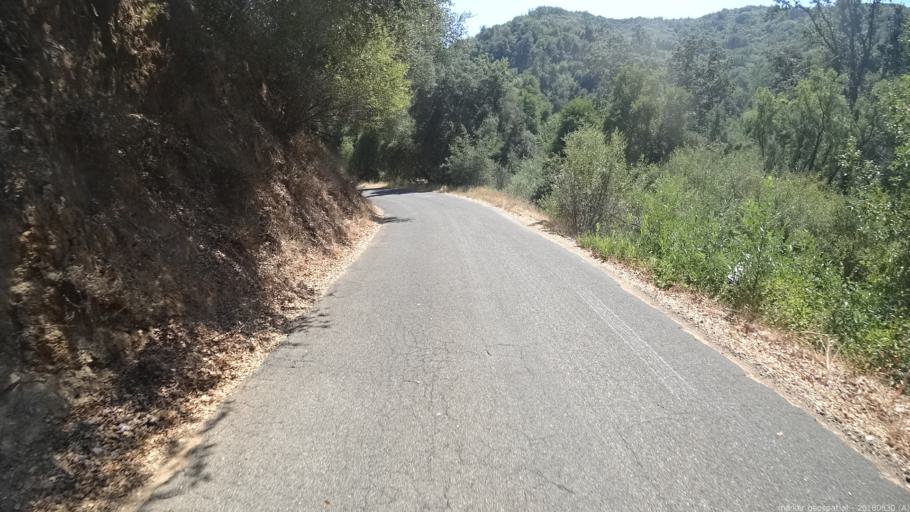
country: US
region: California
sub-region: Monterey County
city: King City
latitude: 36.0045
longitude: -121.3968
